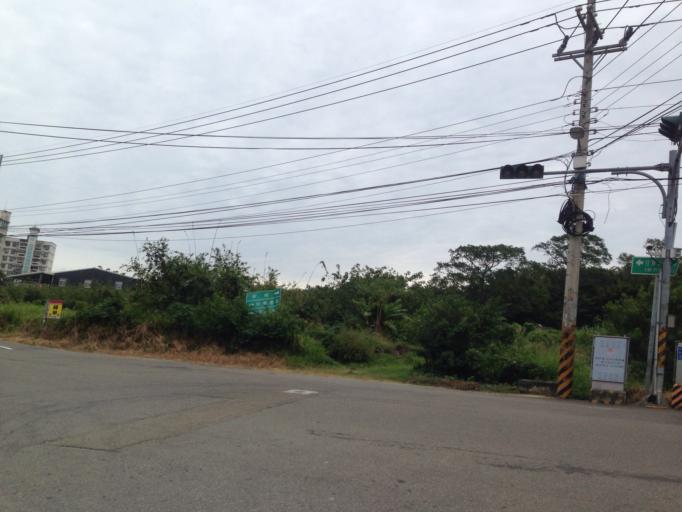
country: TW
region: Taiwan
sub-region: Hsinchu
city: Hsinchu
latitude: 24.7608
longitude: 120.9822
